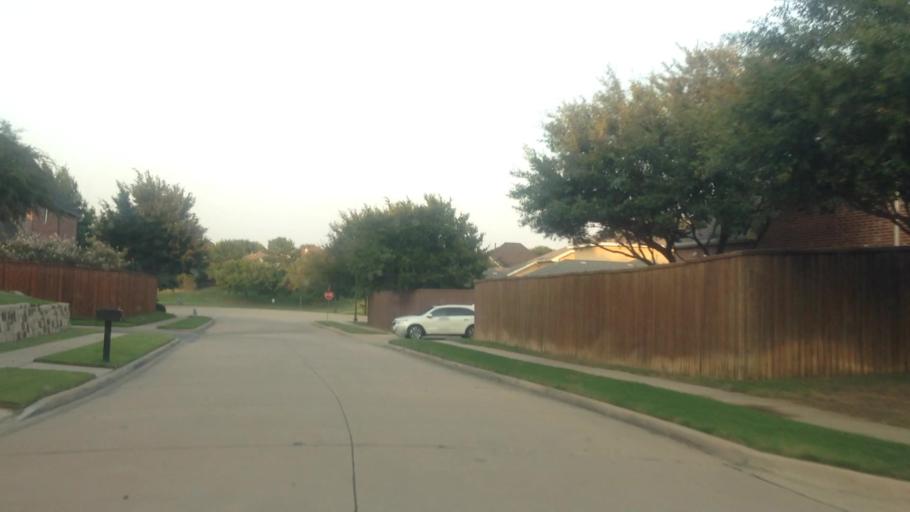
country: US
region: Texas
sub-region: Denton County
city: The Colony
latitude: 33.1244
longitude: -96.8802
